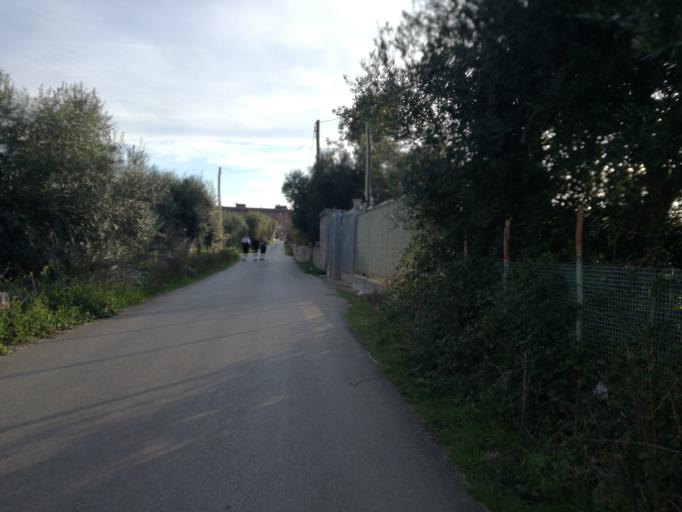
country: IT
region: Apulia
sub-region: Provincia di Bari
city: Valenzano
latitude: 41.0494
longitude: 16.8906
